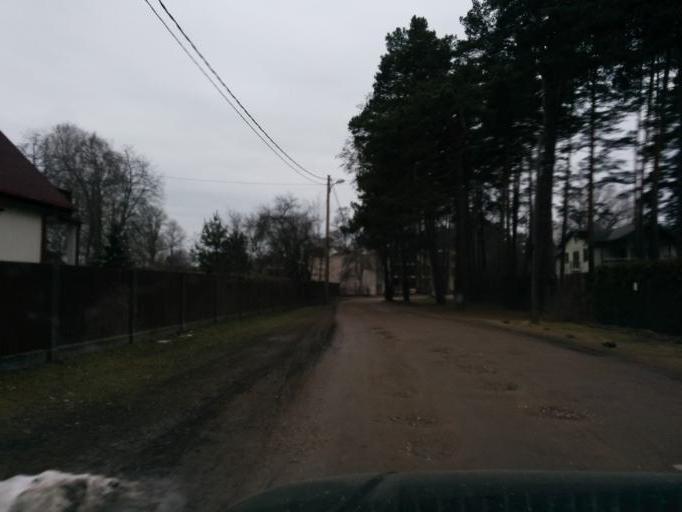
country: LV
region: Jurmala
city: Jurmala
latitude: 56.9669
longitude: 23.8366
